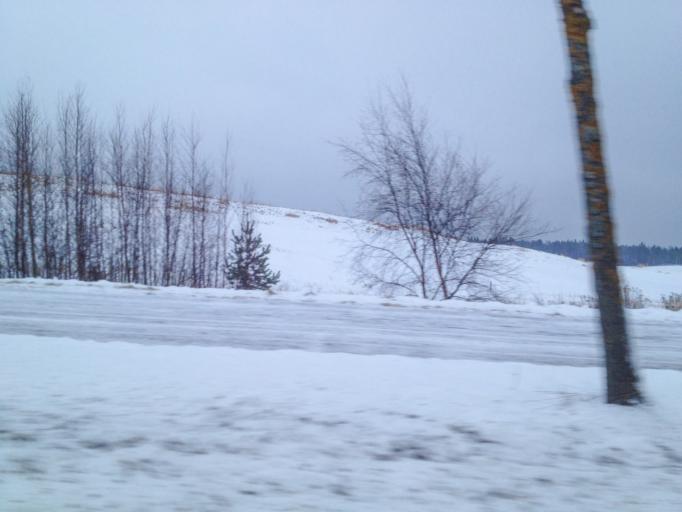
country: FI
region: Uusimaa
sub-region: Helsinki
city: Vantaa
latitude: 60.2118
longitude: 25.1657
